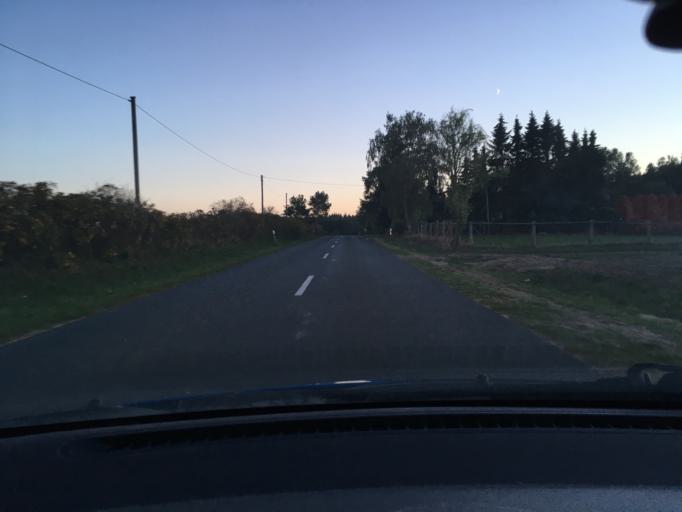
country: DE
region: Lower Saxony
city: Reinstorf
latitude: 53.2274
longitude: 10.5708
